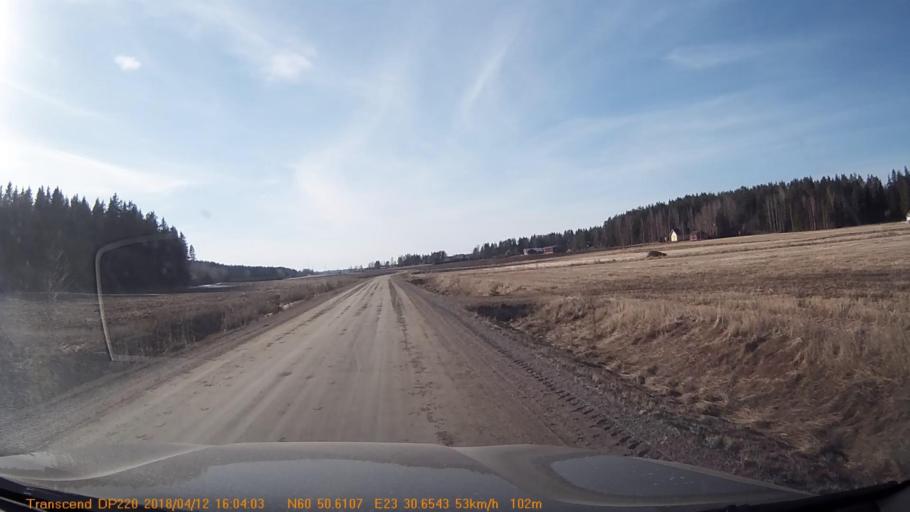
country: FI
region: Haeme
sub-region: Forssa
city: Jokioinen
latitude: 60.8436
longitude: 23.5106
